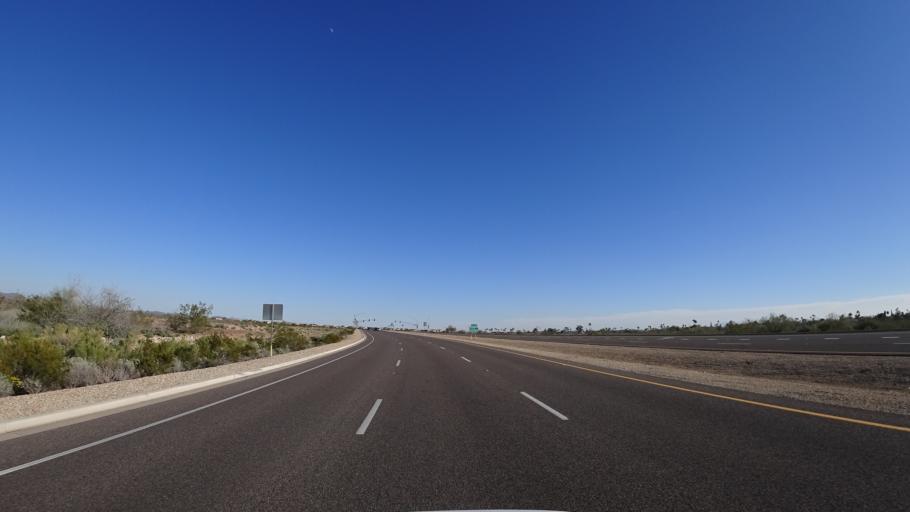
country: US
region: Arizona
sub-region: Maricopa County
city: Sun City West
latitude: 33.6856
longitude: -112.3315
